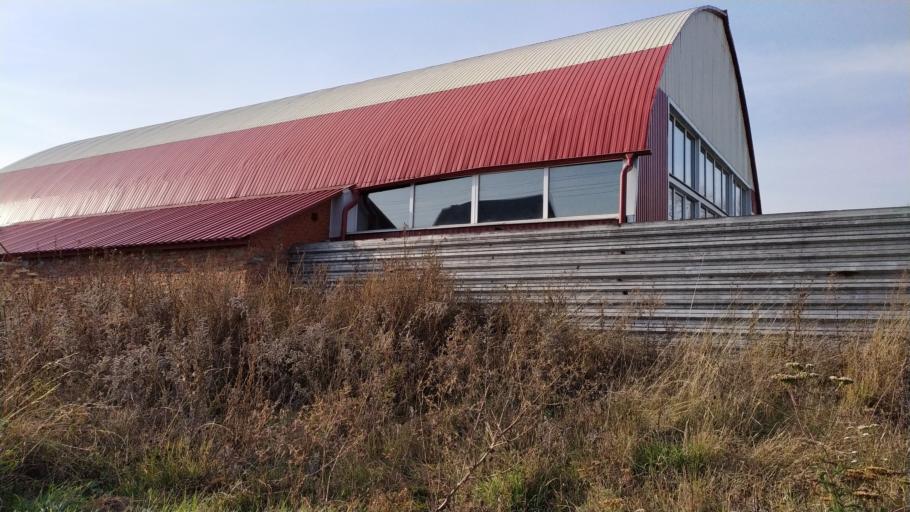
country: RU
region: Kursk
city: Kursk
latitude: 51.6414
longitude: 36.1512
